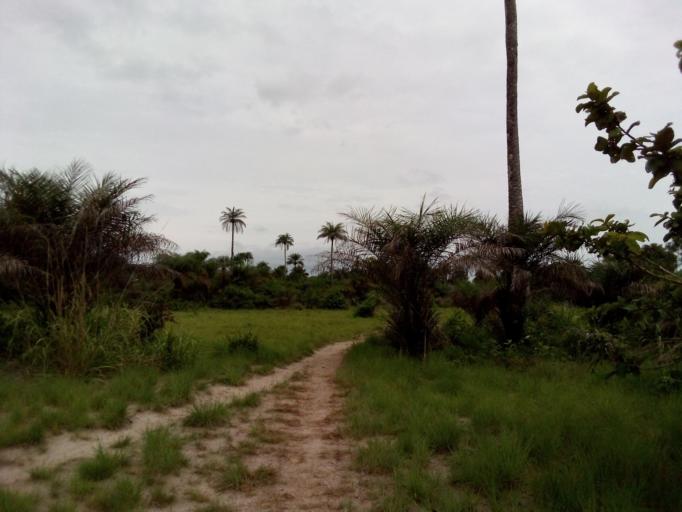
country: SL
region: Southern Province
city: Bonthe
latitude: 7.5207
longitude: -12.5754
